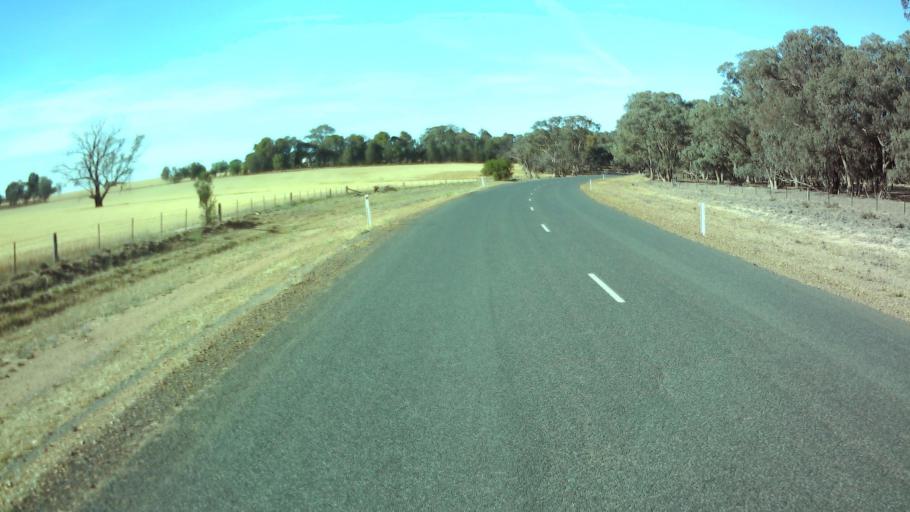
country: AU
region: New South Wales
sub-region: Weddin
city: Grenfell
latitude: -33.9870
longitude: 148.1404
